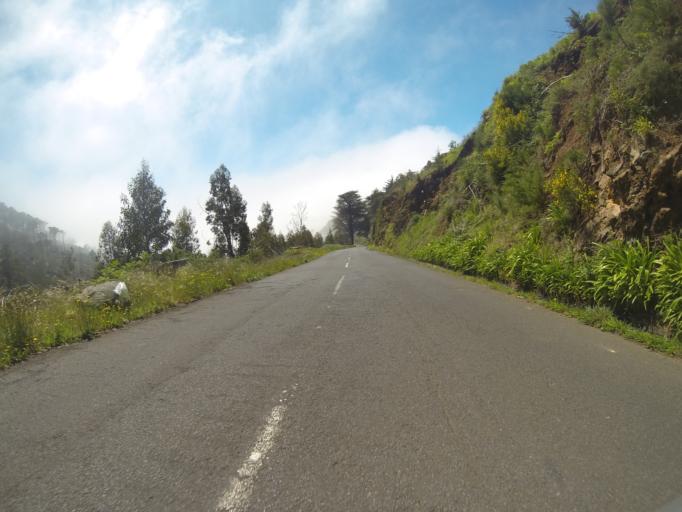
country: PT
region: Madeira
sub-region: Funchal
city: Nossa Senhora do Monte
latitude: 32.6927
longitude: -16.9004
